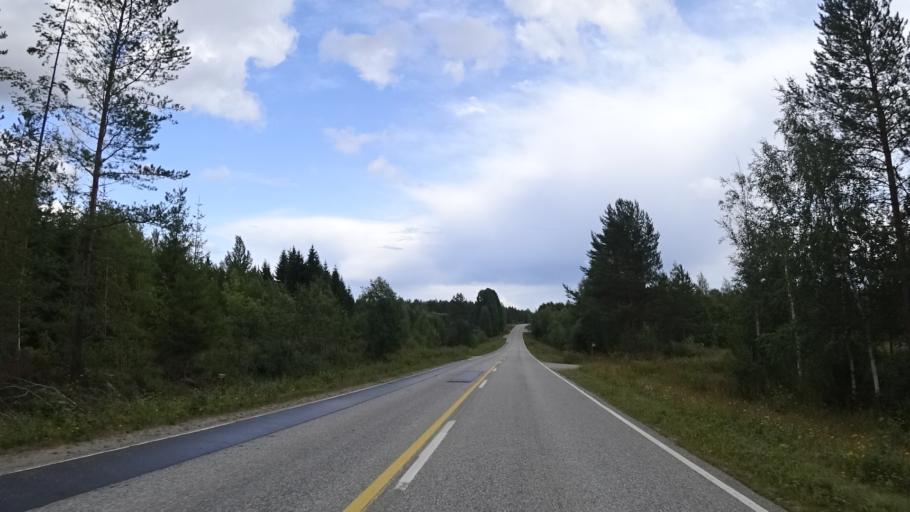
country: FI
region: North Karelia
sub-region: Joensuu
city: Ilomantsi
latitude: 62.6479
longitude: 31.0229
